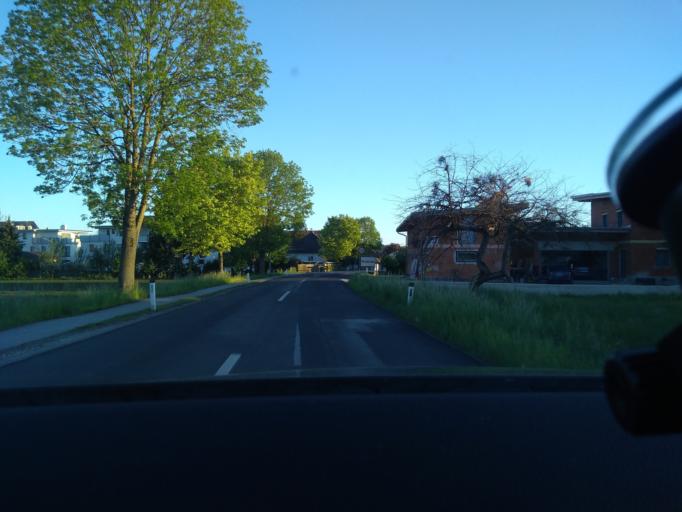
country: AT
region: Styria
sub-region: Politischer Bezirk Voitsberg
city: Mooskirchen
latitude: 46.9894
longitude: 15.2823
